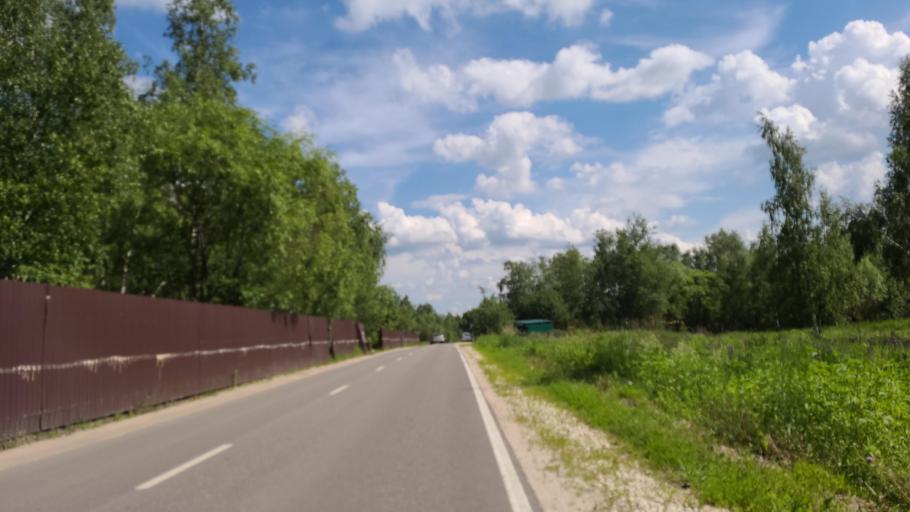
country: RU
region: Moskovskaya
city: Konobeyevo
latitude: 55.3995
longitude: 38.6788
